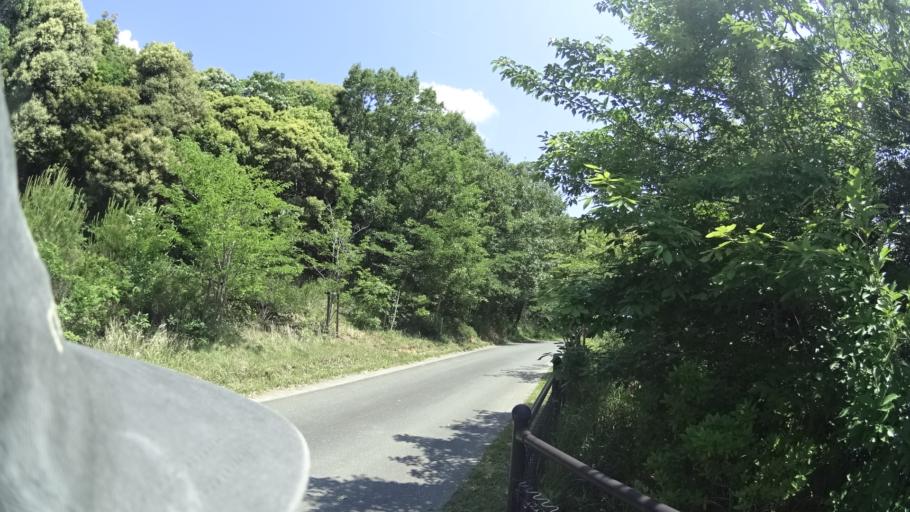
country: JP
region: Shizuoka
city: Kosai-shi
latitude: 34.7368
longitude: 137.4823
